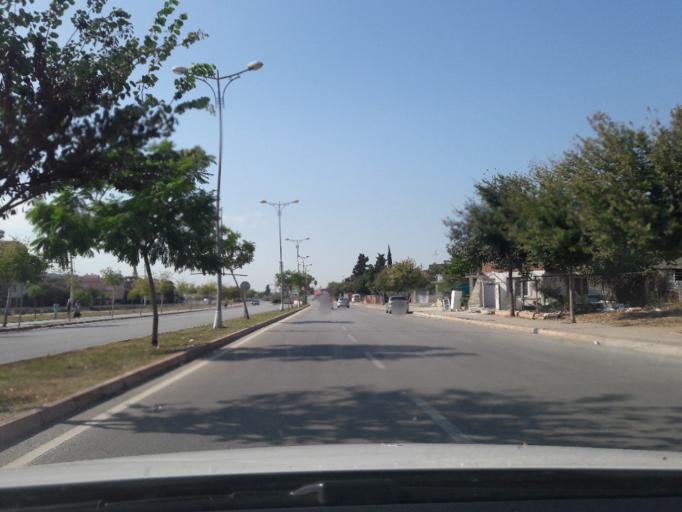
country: TR
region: Adana
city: Seyhan
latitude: 36.9993
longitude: 35.3043
